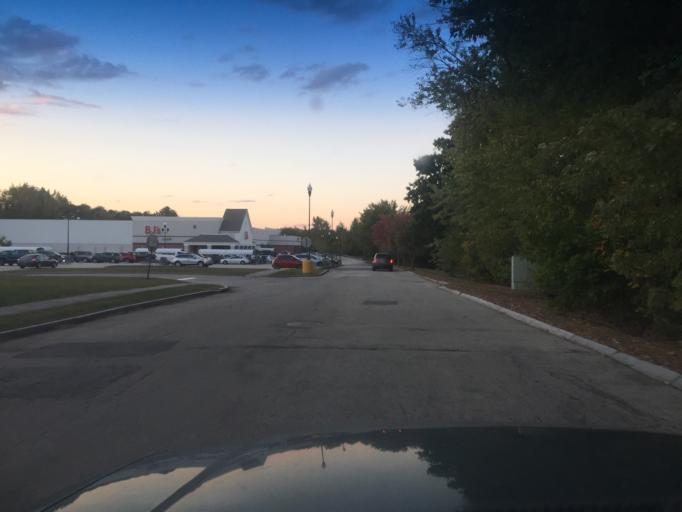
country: US
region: Massachusetts
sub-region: Norfolk County
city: Franklin
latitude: 42.0924
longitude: -71.4340
